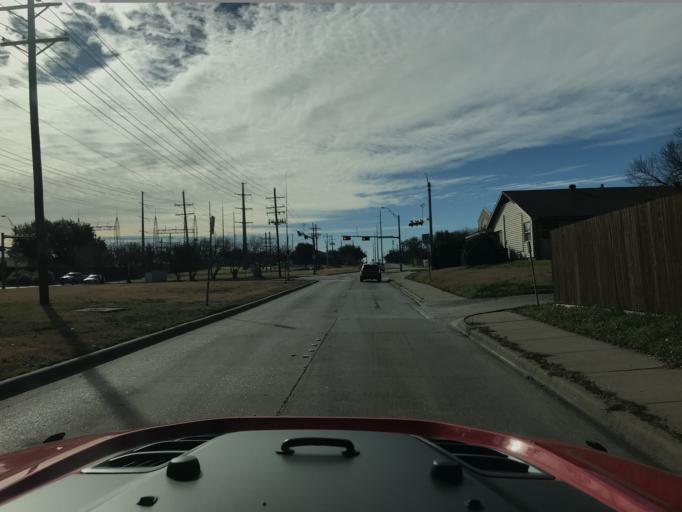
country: US
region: Texas
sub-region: Denton County
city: Lewisville
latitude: 33.0500
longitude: -97.0359
